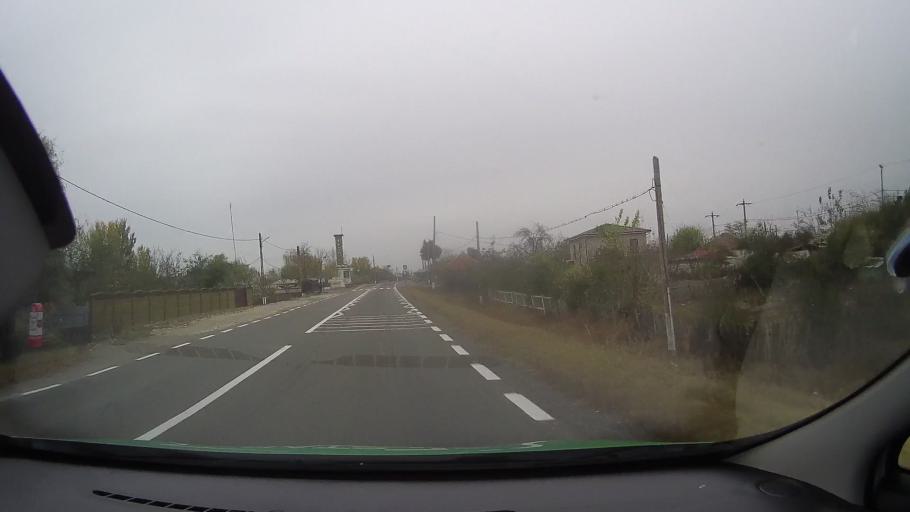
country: RO
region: Ialomita
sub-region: Comuna Giurgeni
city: Giurgeni
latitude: 44.7454
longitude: 27.8568
